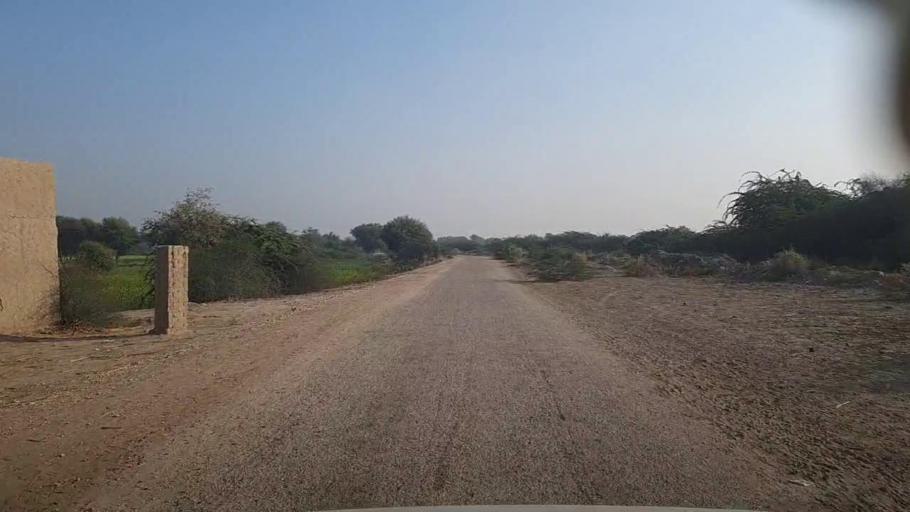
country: PK
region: Sindh
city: Karaundi
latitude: 26.7413
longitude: 68.4776
